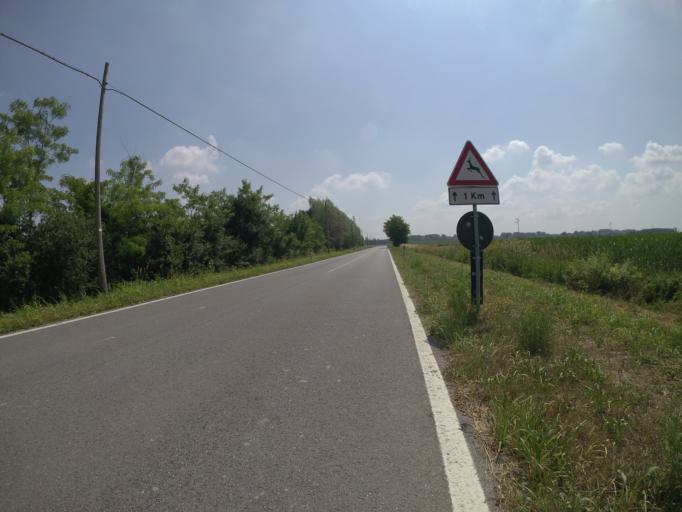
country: IT
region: Friuli Venezia Giulia
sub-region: Provincia di Udine
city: Teor
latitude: 45.8712
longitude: 13.0682
